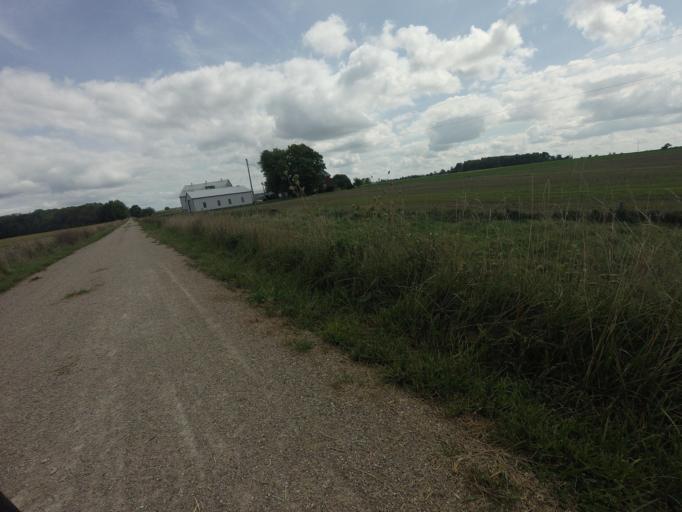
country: CA
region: Ontario
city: North Perth
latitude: 43.5702
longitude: -80.8921
